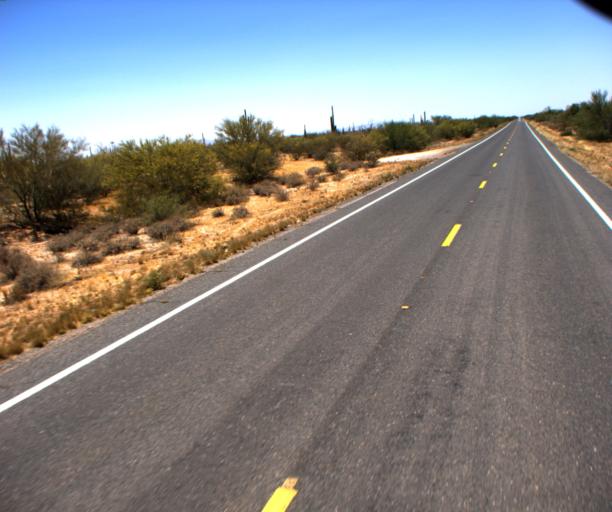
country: US
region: Arizona
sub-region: Pinal County
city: Florence
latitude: 32.8582
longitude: -111.2381
